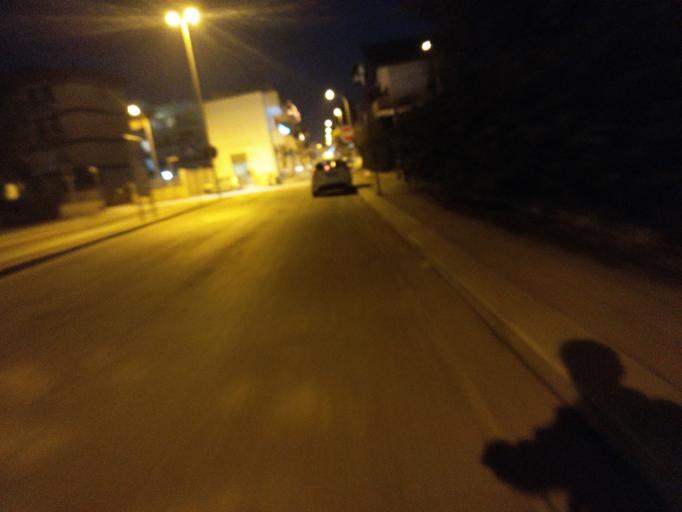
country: IT
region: Apulia
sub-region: Provincia di Bari
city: Modugno
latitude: 41.0801
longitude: 16.7865
